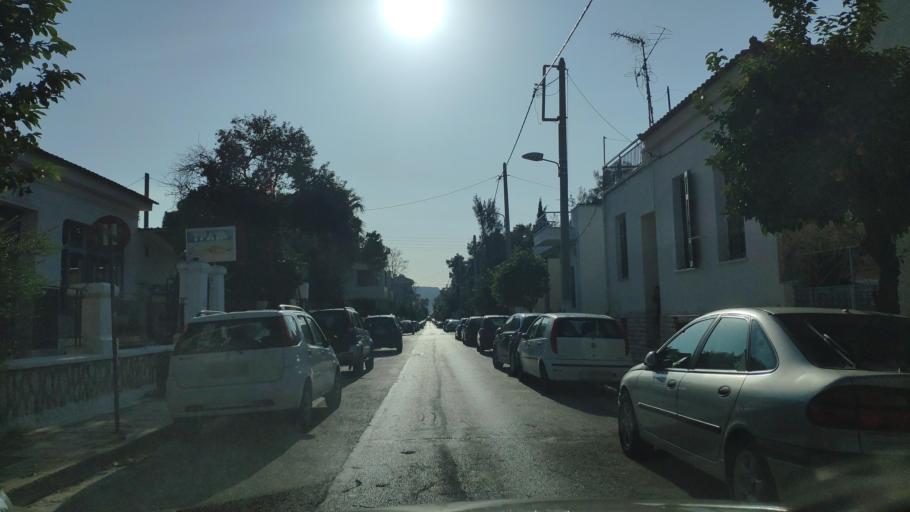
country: GR
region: Attica
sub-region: Nomarchia Dytikis Attikis
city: Elefsina
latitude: 38.0398
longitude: 23.5410
